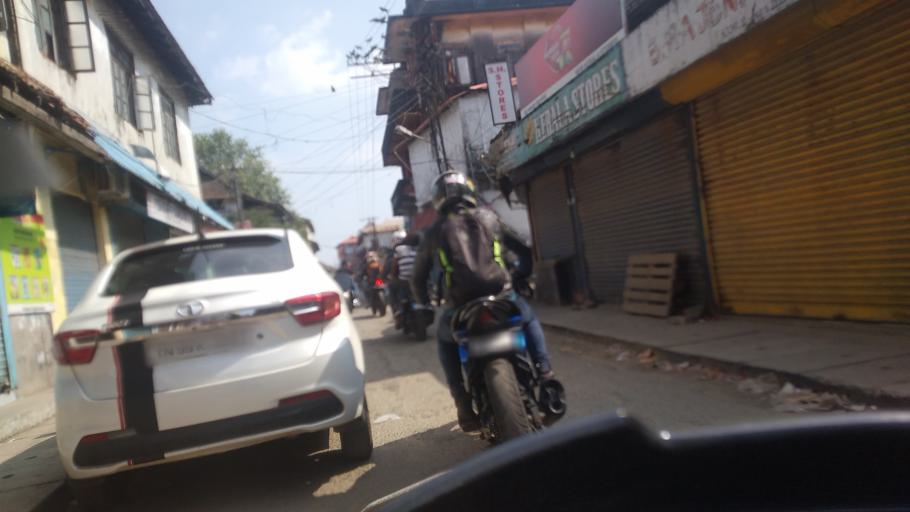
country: IN
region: Kerala
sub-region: Ernakulam
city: Cochin
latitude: 9.9652
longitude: 76.2548
